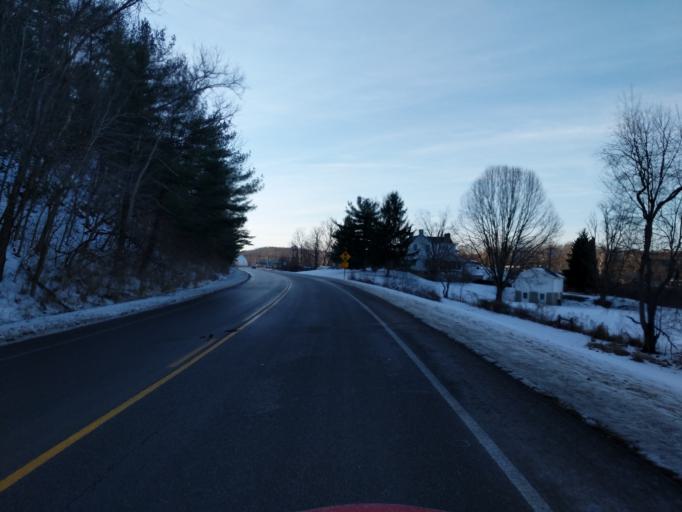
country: US
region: Ohio
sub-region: Athens County
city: Athens
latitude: 39.3289
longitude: -82.1237
